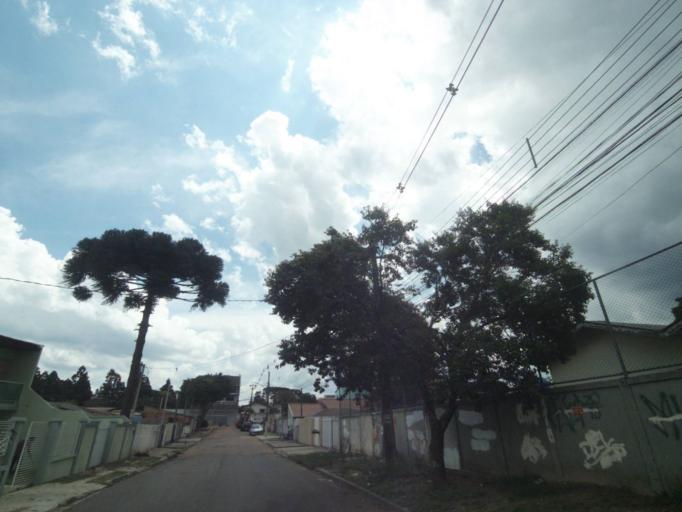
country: BR
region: Parana
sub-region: Curitiba
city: Curitiba
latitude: -25.4653
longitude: -49.3420
